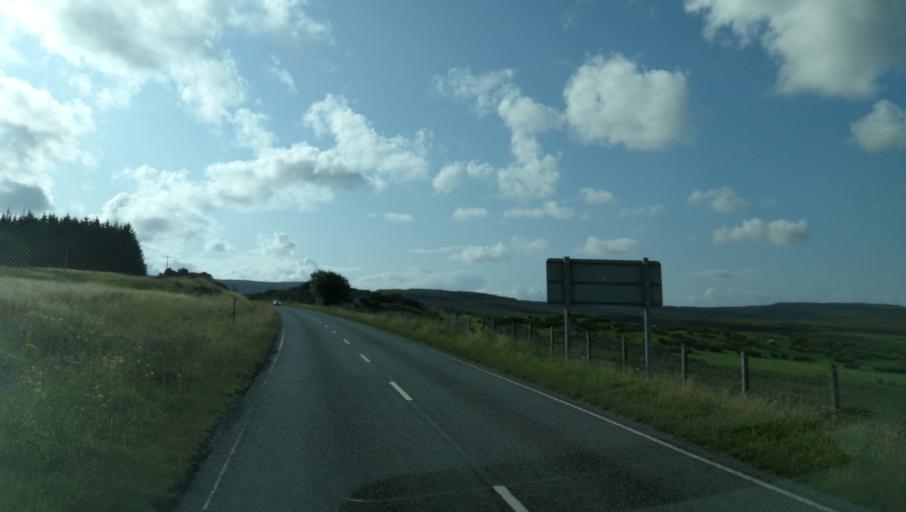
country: GB
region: Scotland
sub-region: Highland
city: Isle of Skye
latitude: 57.4716
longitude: -6.4400
